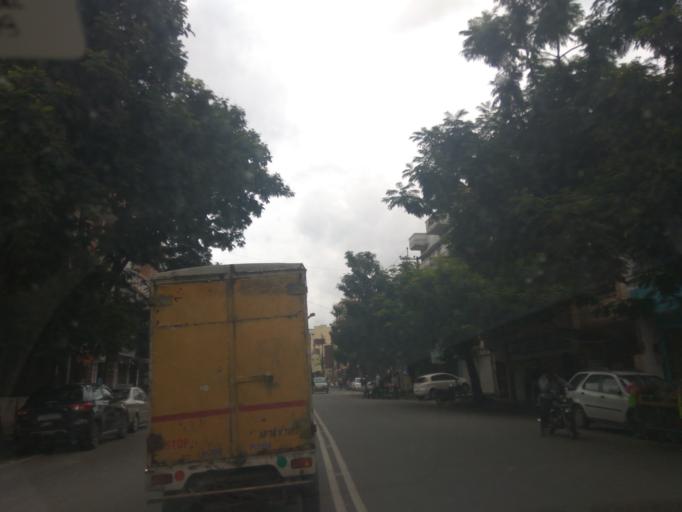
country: IN
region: Telangana
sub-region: Hyderabad
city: Hyderabad
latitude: 17.3958
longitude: 78.4887
